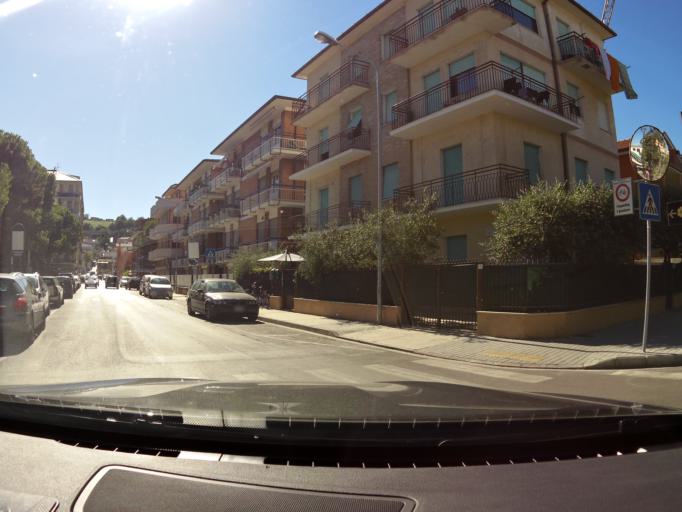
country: IT
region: The Marches
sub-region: Province of Fermo
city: Porto San Giorgio
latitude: 43.1878
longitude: 13.7930
